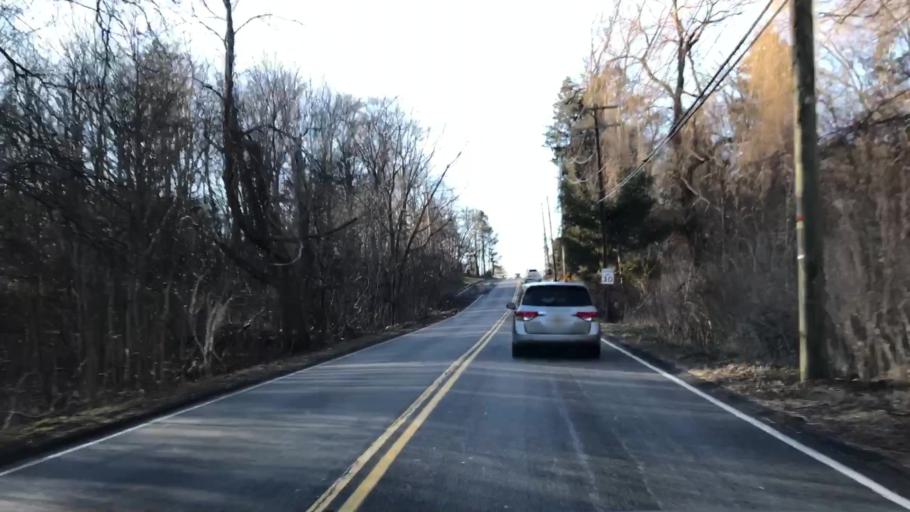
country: US
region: New York
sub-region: Rockland County
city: New Hempstead
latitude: 41.1493
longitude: -74.0295
